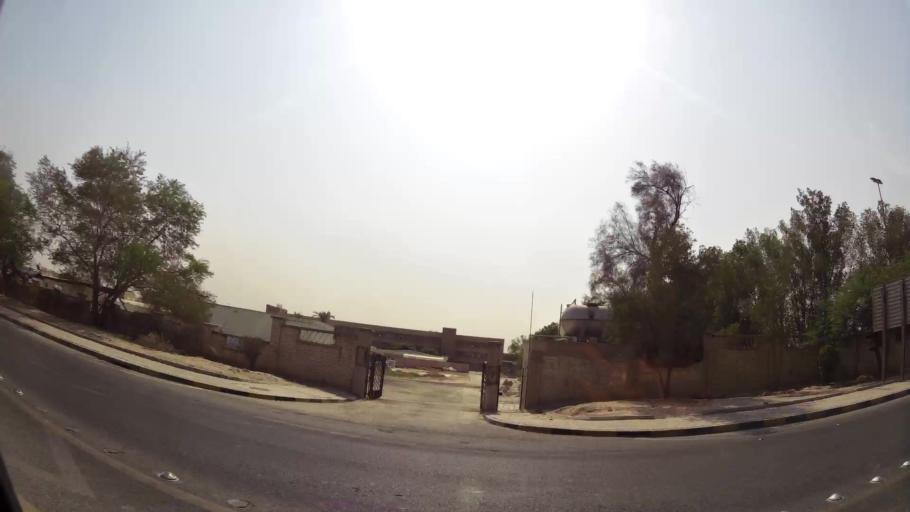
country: KW
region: Al Asimah
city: Ash Shamiyah
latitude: 29.3435
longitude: 47.9708
